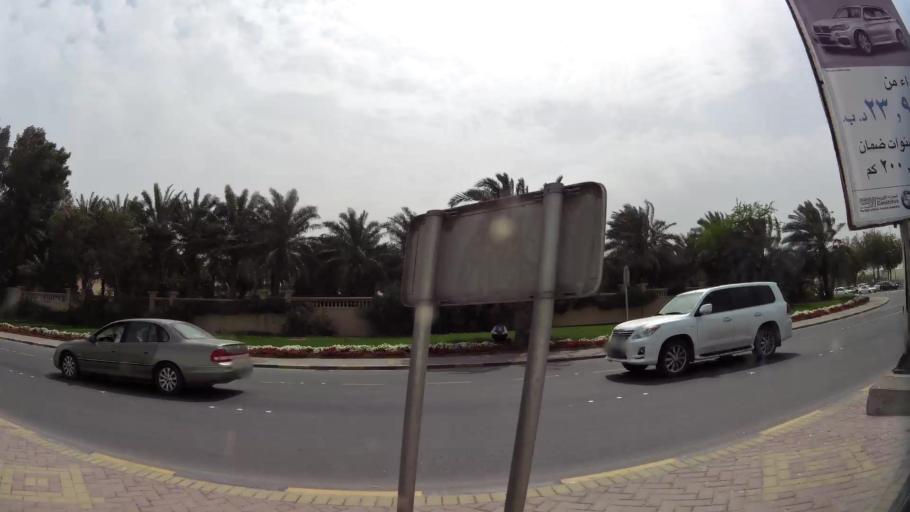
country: BH
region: Northern
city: Ar Rifa'
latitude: 26.1335
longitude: 50.5386
